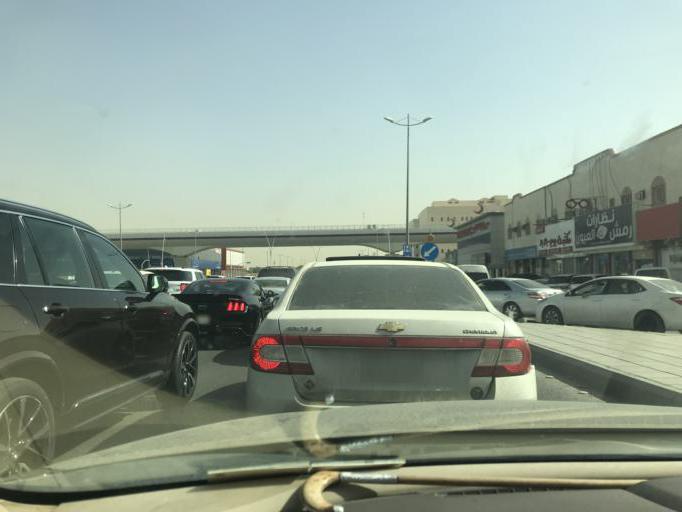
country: SA
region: Ar Riyad
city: Riyadh
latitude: 24.7939
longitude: 46.7433
